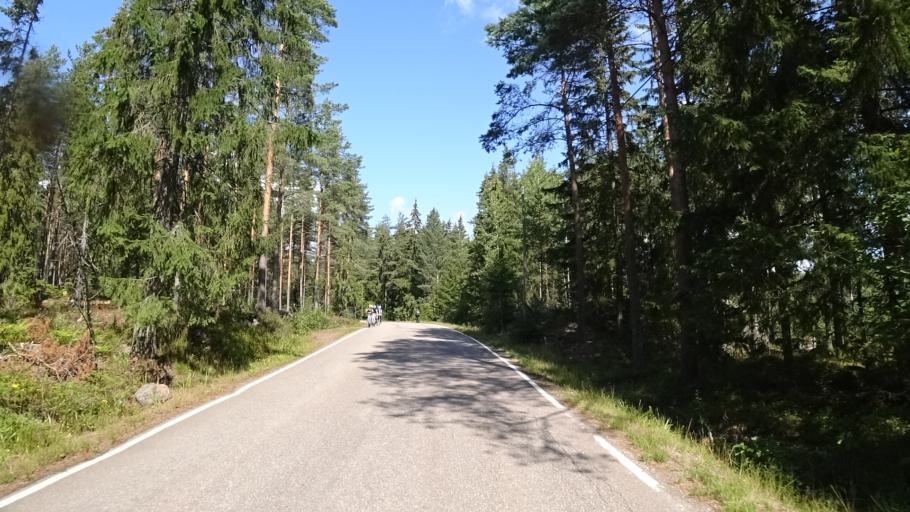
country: FI
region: Kymenlaakso
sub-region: Kotka-Hamina
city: Karhula
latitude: 60.5624
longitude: 26.9015
